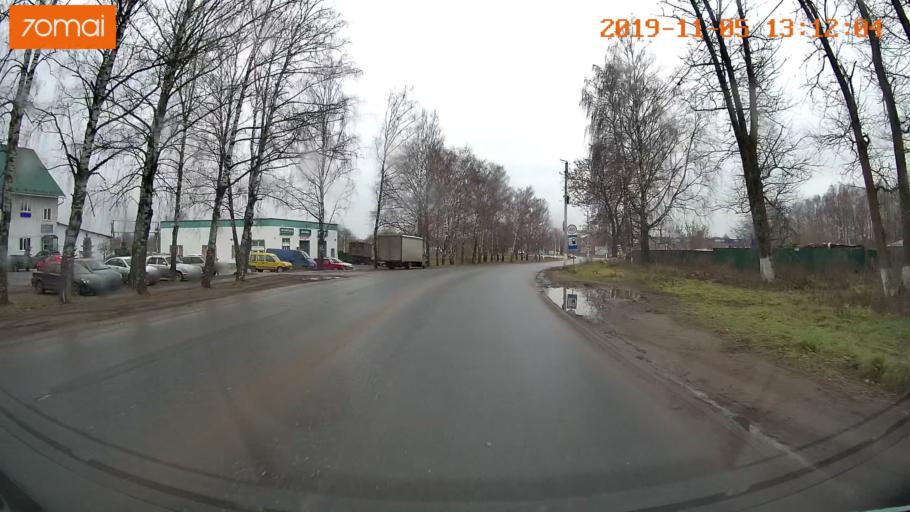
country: RU
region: Ivanovo
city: Shuya
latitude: 56.8576
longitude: 41.3484
